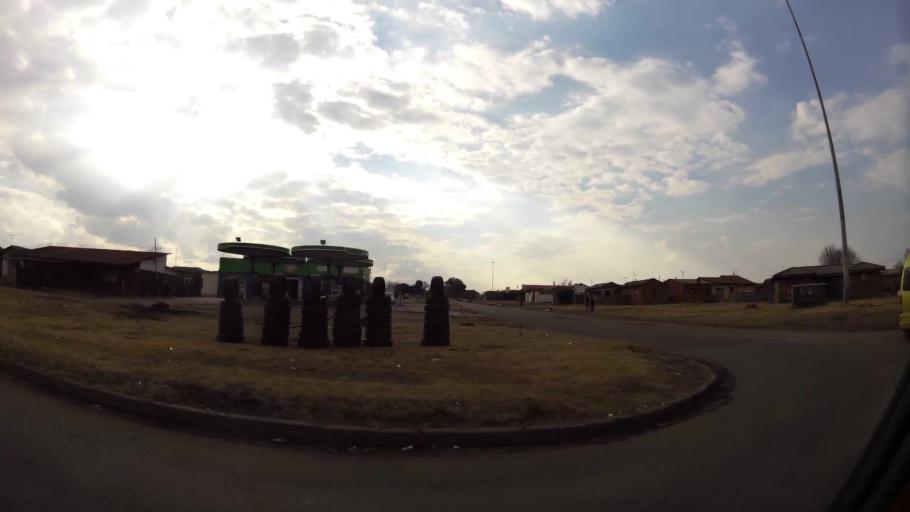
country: ZA
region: Gauteng
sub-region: Sedibeng District Municipality
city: Vereeniging
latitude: -26.6784
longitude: 27.8882
